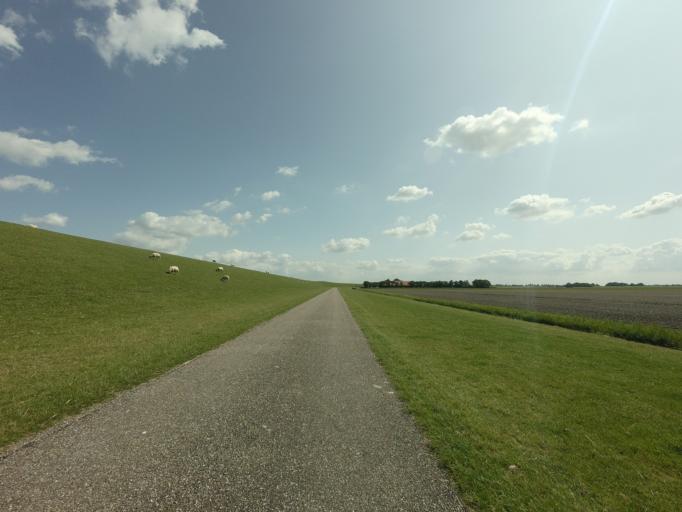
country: NL
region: Friesland
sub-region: Gemeente Ferwerderadiel
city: Hallum
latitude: 53.3240
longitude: 5.7344
